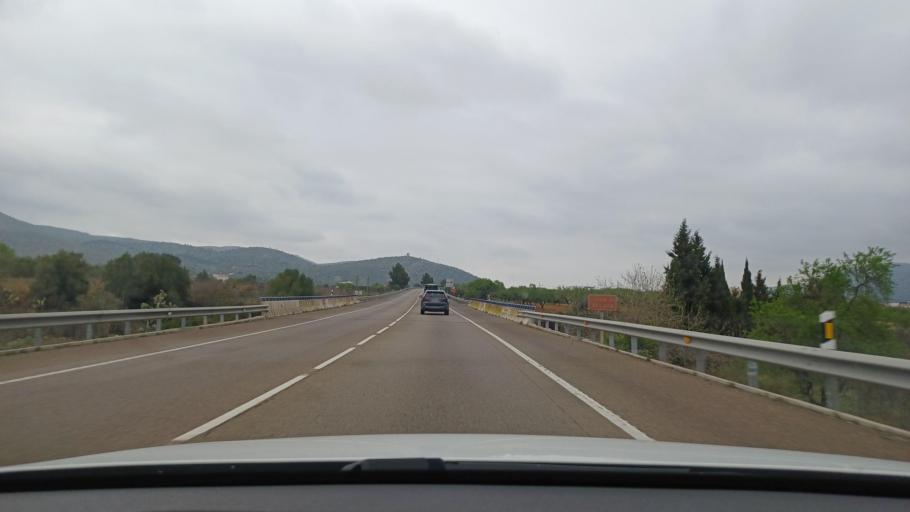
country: ES
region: Valencia
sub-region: Provincia de Castello
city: Santa Magdalena de Pulpis
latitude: 40.3558
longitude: 0.2969
